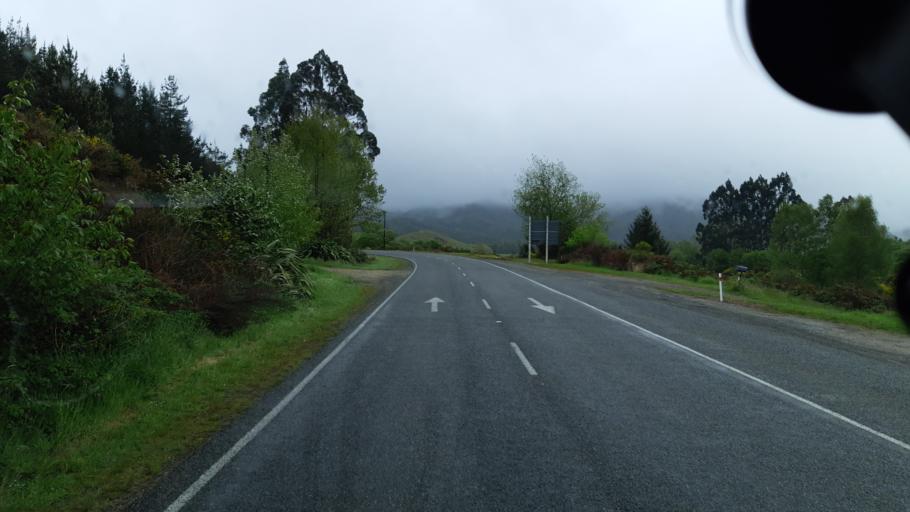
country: NZ
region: West Coast
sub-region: Buller District
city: Westport
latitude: -42.1217
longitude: 171.8604
